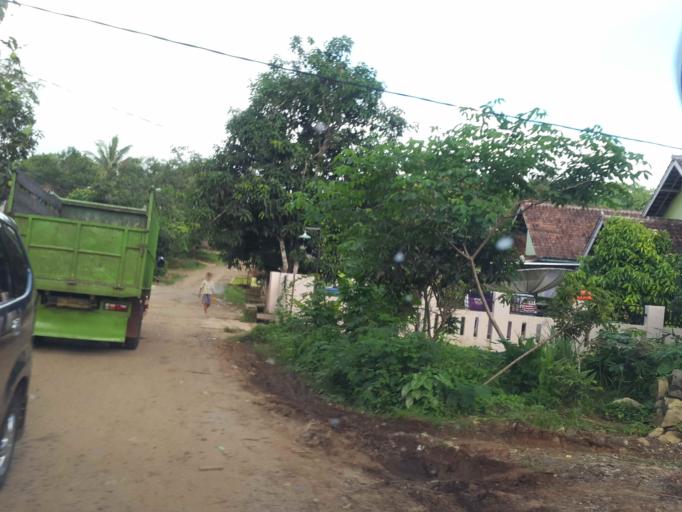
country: ID
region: Banten
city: Cibaliung
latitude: -6.7054
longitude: 105.7173
